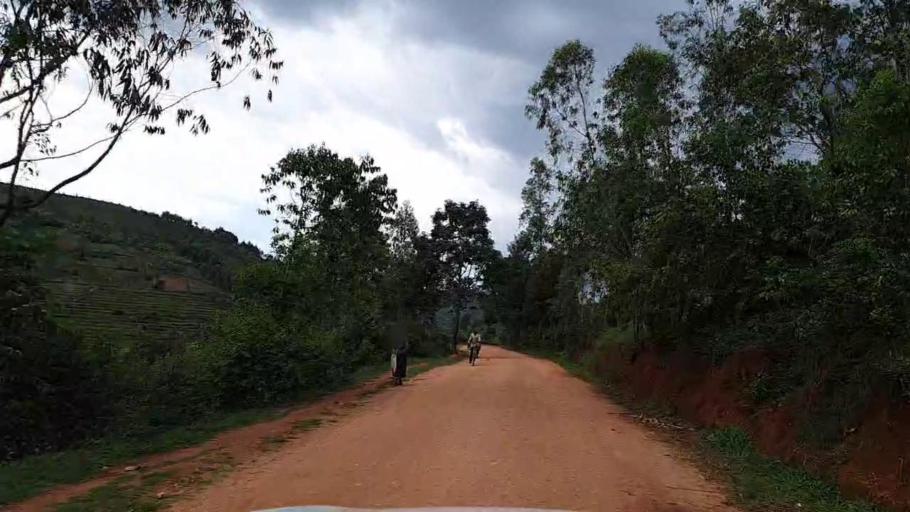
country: RW
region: Southern Province
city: Nyanza
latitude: -2.3922
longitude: 29.6856
